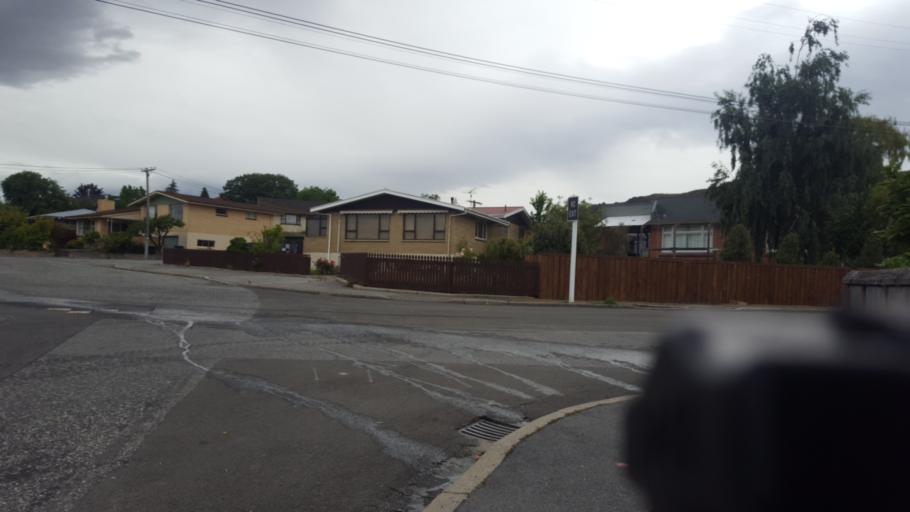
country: NZ
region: Otago
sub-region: Queenstown-Lakes District
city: Wanaka
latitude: -45.2524
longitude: 169.3967
